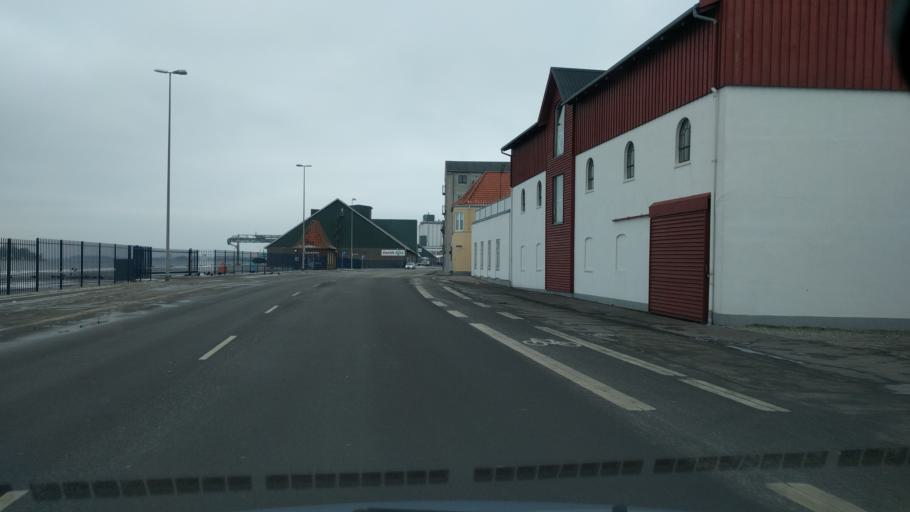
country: DK
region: Zealand
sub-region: Guldborgsund Kommune
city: Nykobing Falster
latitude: 54.7647
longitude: 11.8656
